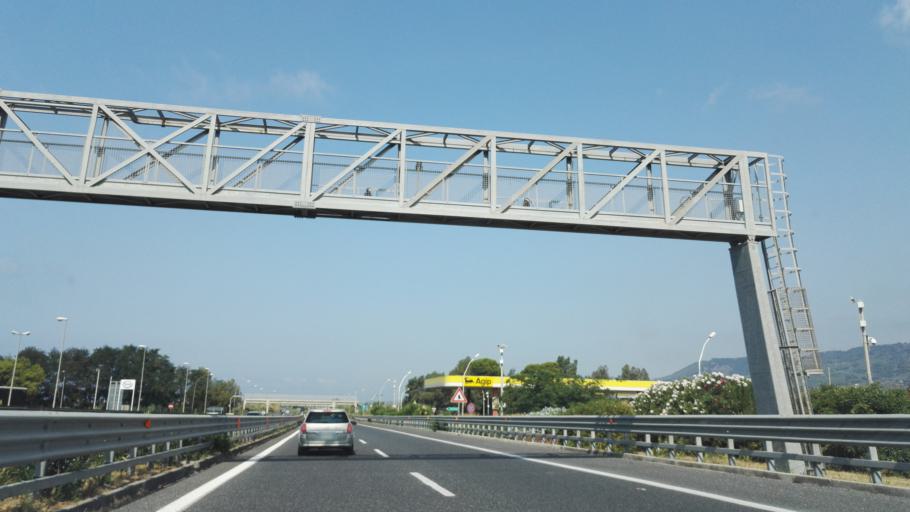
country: IT
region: Calabria
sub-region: Provincia di Catanzaro
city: Santa Eufemia Lamezia
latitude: 38.9296
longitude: 16.2377
